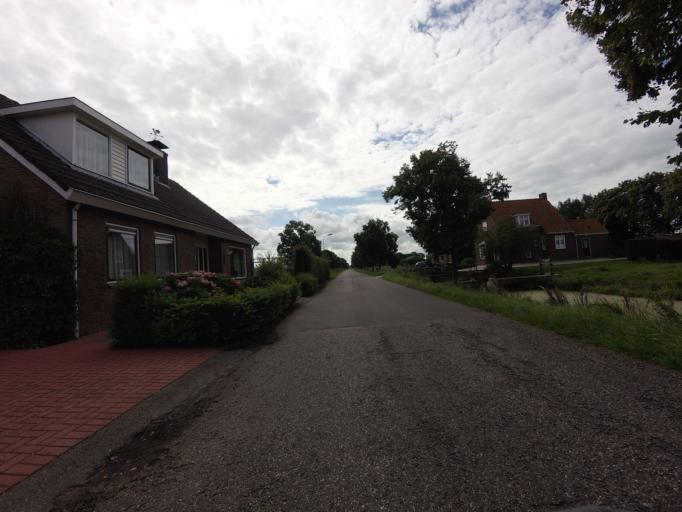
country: NL
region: Utrecht
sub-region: Gemeente Oudewater
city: Oudewater
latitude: 52.0162
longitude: 4.8747
